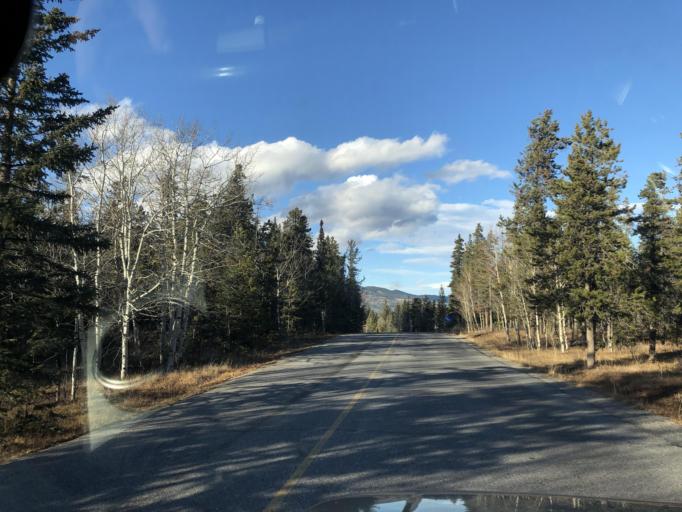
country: CA
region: Alberta
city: Canmore
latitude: 51.0804
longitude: -115.0631
